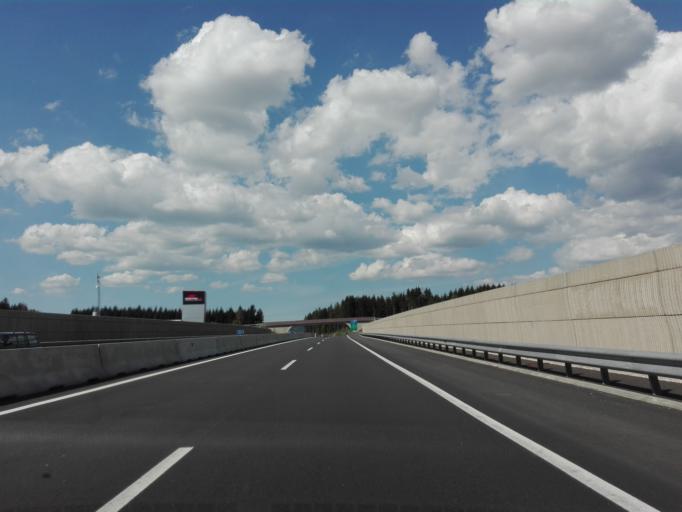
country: AT
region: Upper Austria
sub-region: Politischer Bezirk Freistadt
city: Freistadt
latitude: 48.4743
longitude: 14.5014
